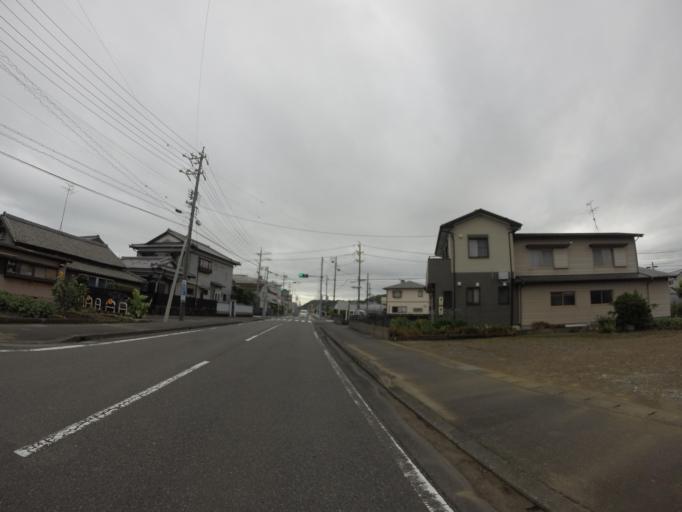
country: JP
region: Shizuoka
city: Sagara
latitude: 34.7575
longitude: 138.2391
